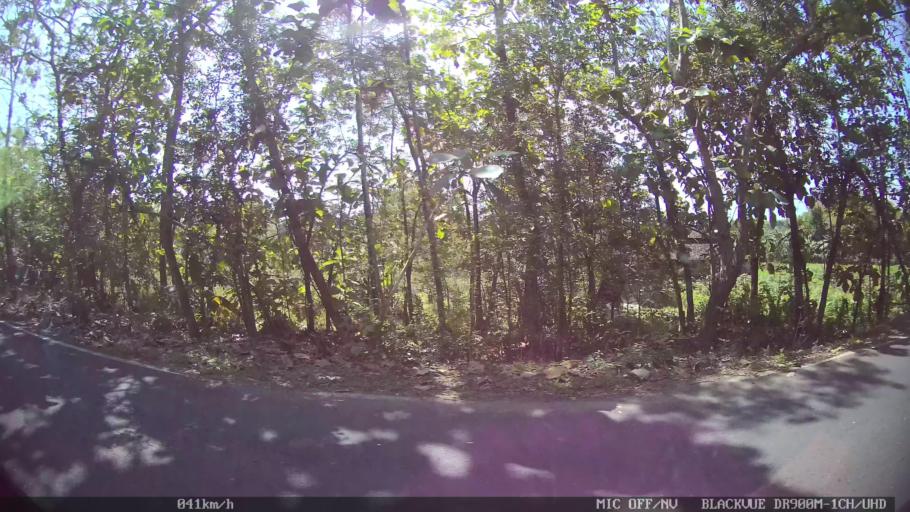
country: ID
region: Daerah Istimewa Yogyakarta
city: Pundong
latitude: -7.9571
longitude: 110.3671
